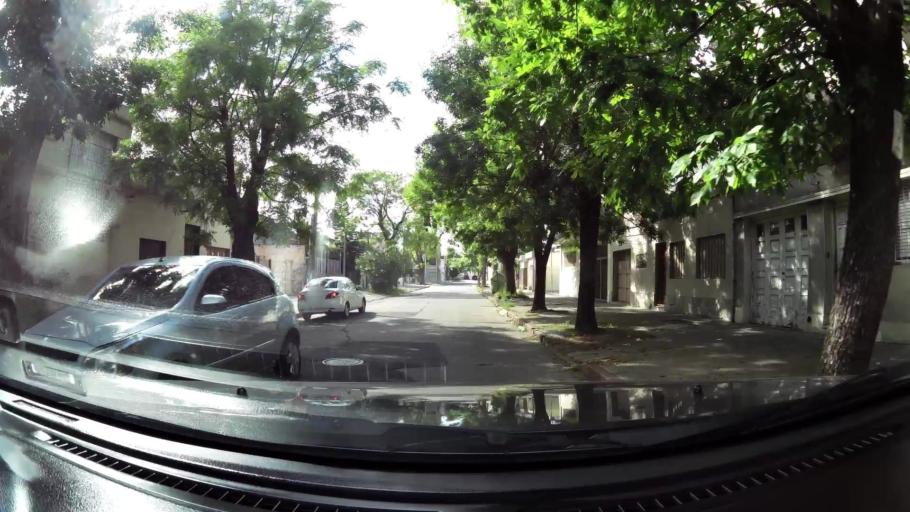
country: UY
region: Montevideo
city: Montevideo
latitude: -34.8843
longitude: -56.1644
